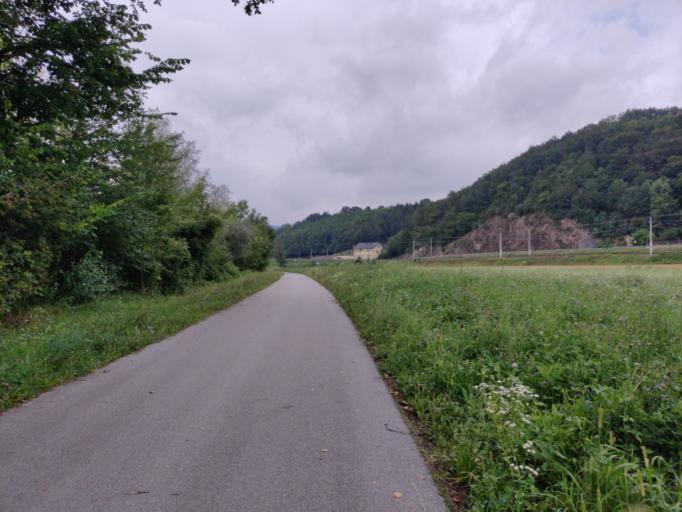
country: AT
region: Lower Austria
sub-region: Politischer Bezirk Melk
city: Ybbs an der Donau
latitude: 48.1810
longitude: 15.1207
